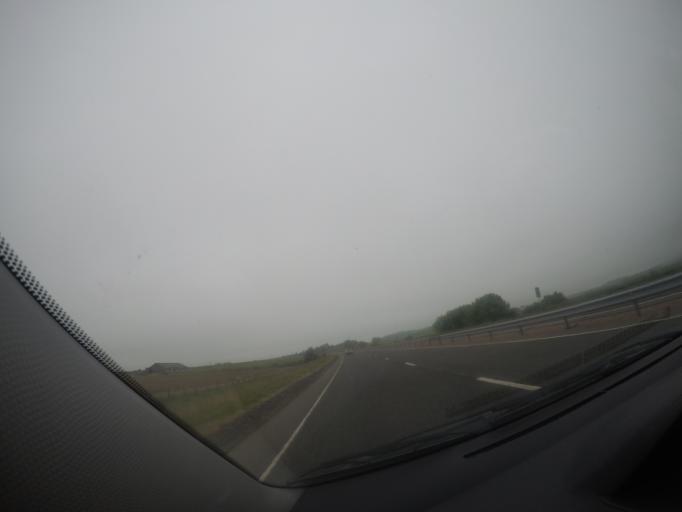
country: GB
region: Scotland
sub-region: Angus
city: Forfar
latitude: 56.6102
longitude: -2.9013
